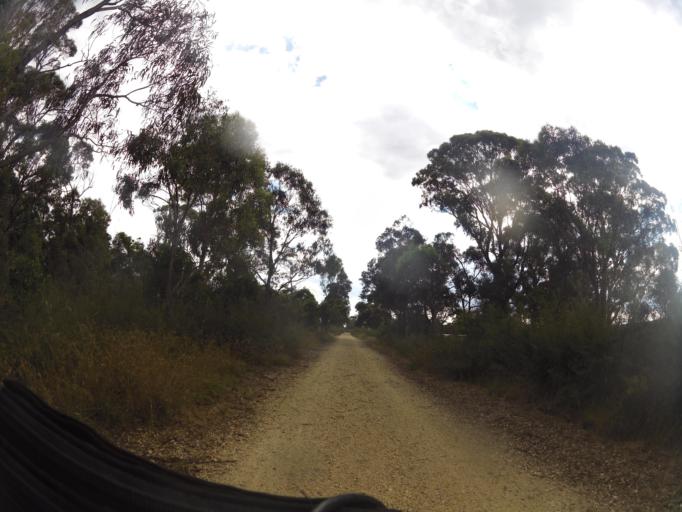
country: AU
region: Victoria
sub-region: Wellington
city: Heyfield
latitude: -38.0439
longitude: 146.6413
